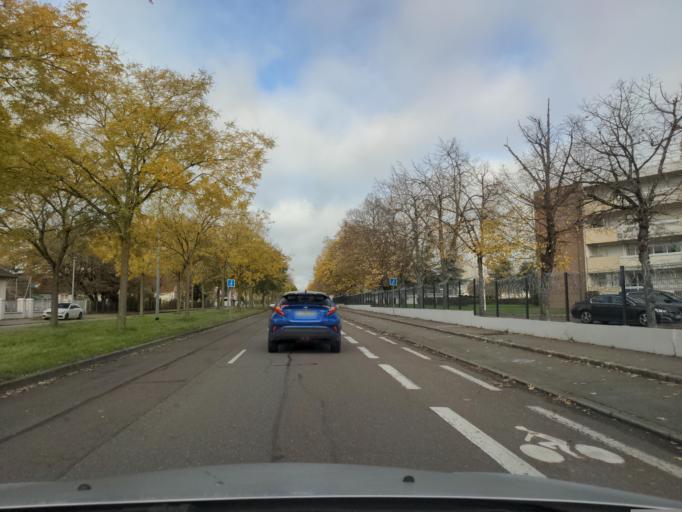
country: FR
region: Bourgogne
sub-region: Departement de la Cote-d'Or
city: Fontaine-les-Dijon
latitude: 47.3420
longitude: 5.0509
